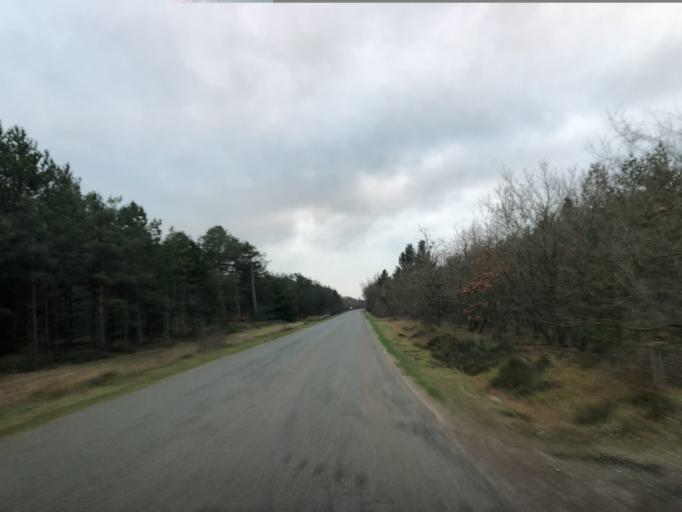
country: DK
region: Central Jutland
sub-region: Holstebro Kommune
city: Ulfborg
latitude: 56.2515
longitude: 8.2821
